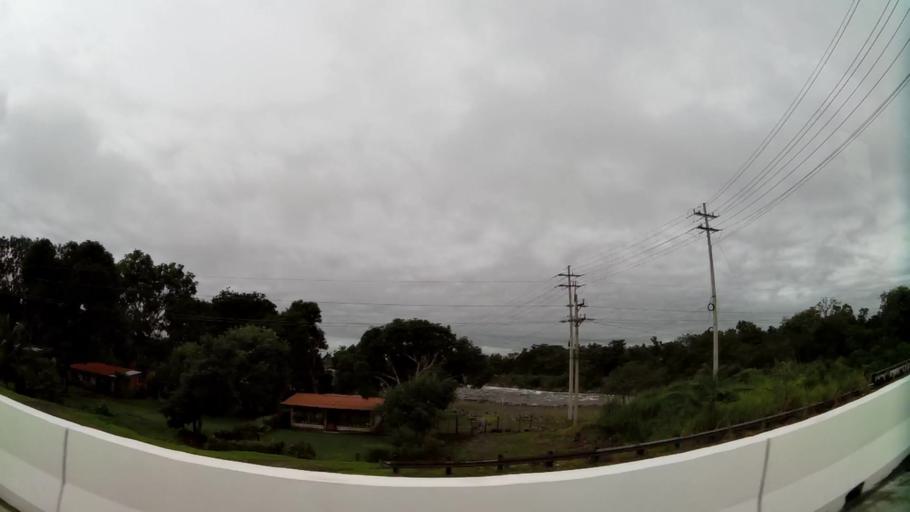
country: PA
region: Chiriqui
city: Bugaba
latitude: 8.4986
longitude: -82.5946
